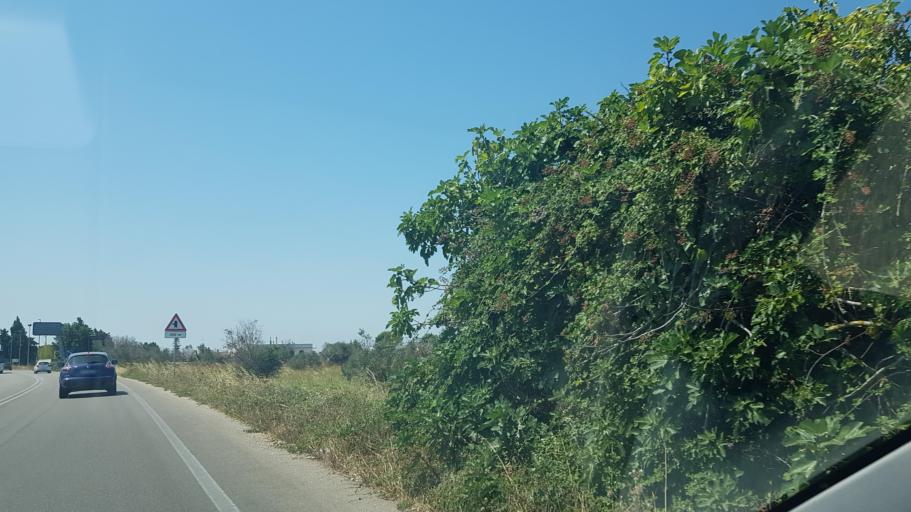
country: IT
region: Apulia
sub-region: Provincia di Lecce
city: Merine
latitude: 40.3378
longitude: 18.2294
